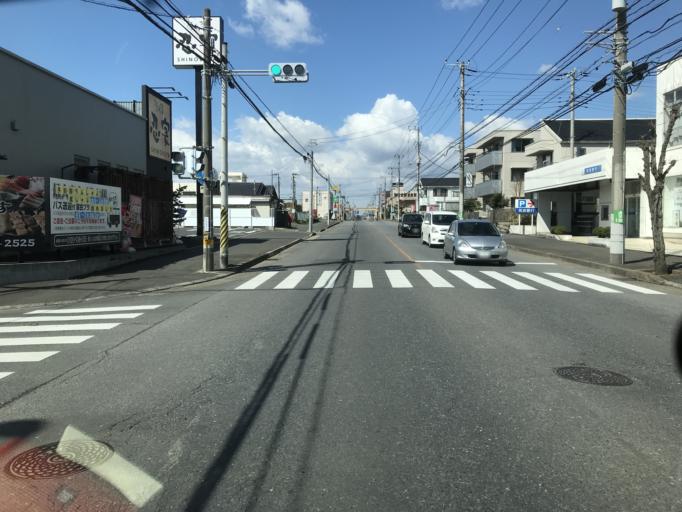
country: JP
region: Ibaraki
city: Ishioka
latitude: 36.1187
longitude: 140.2354
